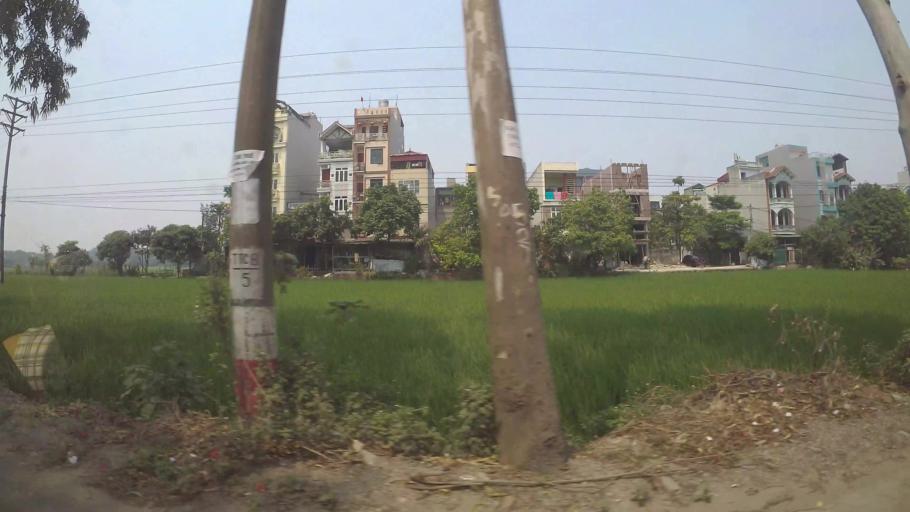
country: VN
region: Ha Noi
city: Van Dien
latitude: 20.9489
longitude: 105.8235
